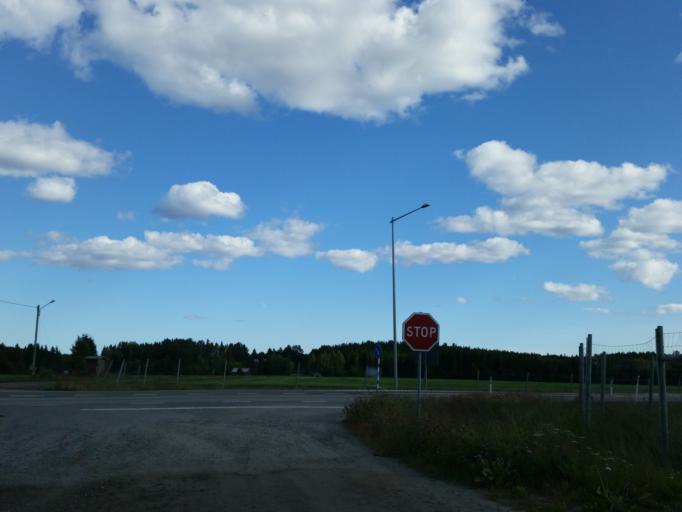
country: SE
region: Vaesterbotten
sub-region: Robertsfors Kommun
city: Robertsfors
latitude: 64.1285
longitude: 20.8873
